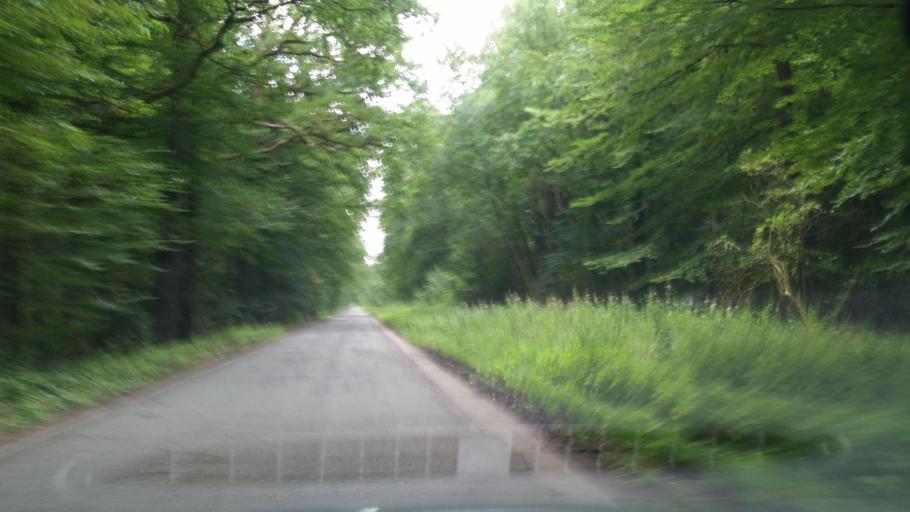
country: DE
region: Lower Saxony
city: Bispingen
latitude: 53.0943
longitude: 9.9069
